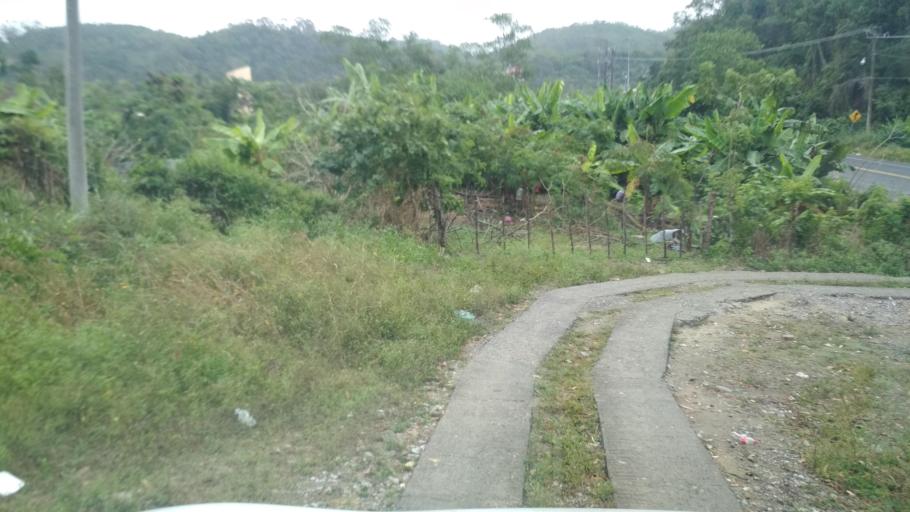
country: MX
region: Veracruz
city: Papantla de Olarte
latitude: 20.4644
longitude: -97.3082
